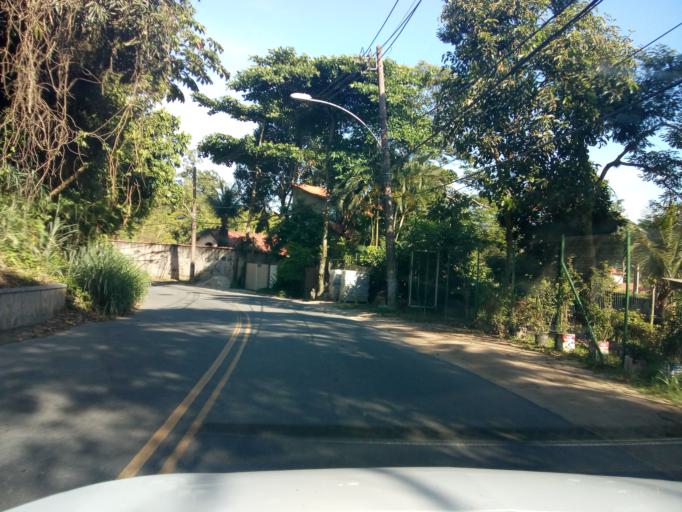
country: BR
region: Rio de Janeiro
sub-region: Nilopolis
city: Nilopolis
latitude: -23.0246
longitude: -43.5013
